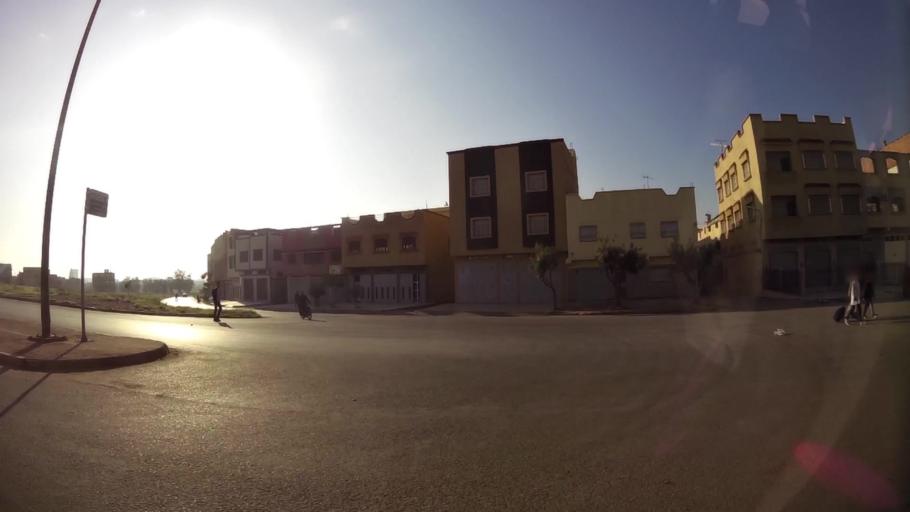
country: MA
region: Oriental
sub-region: Oujda-Angad
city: Oujda
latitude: 34.6734
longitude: -1.9398
